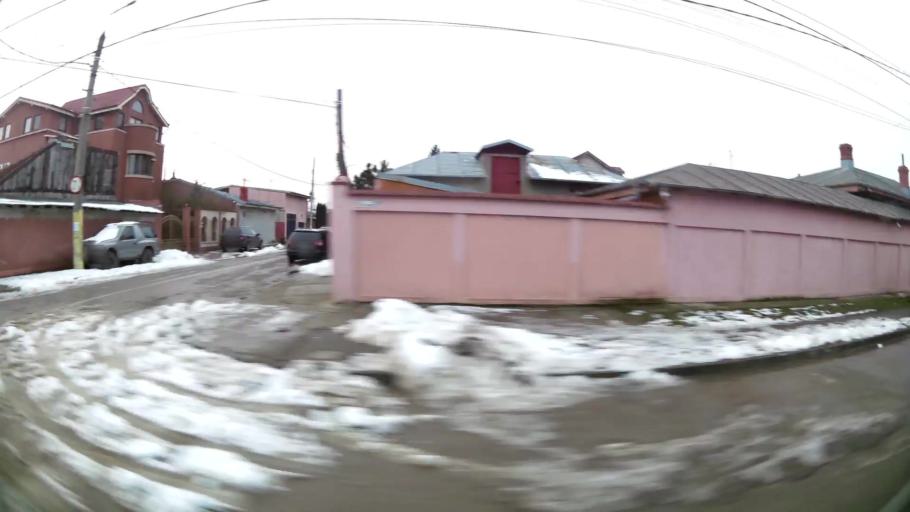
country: RO
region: Ilfov
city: Dobroesti
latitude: 44.4560
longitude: 26.1853
